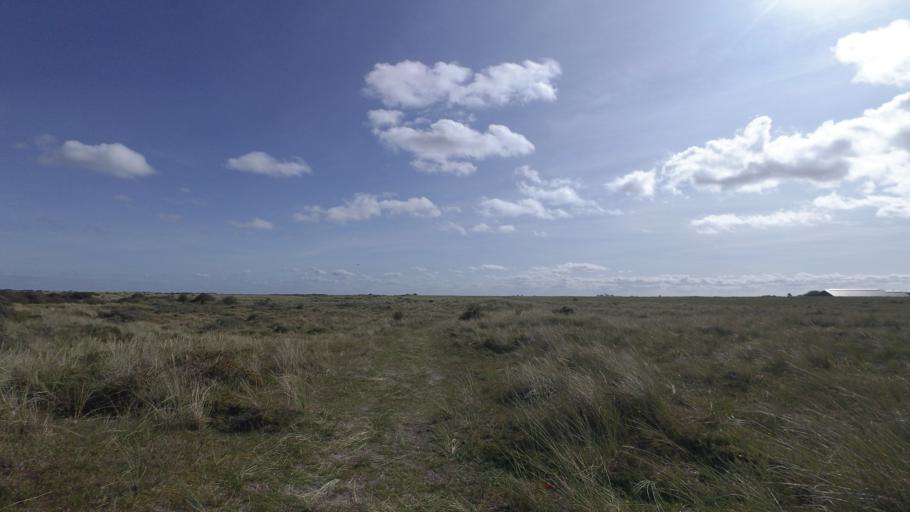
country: NL
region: Friesland
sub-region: Gemeente Ameland
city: Nes
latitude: 53.4517
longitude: 5.7318
